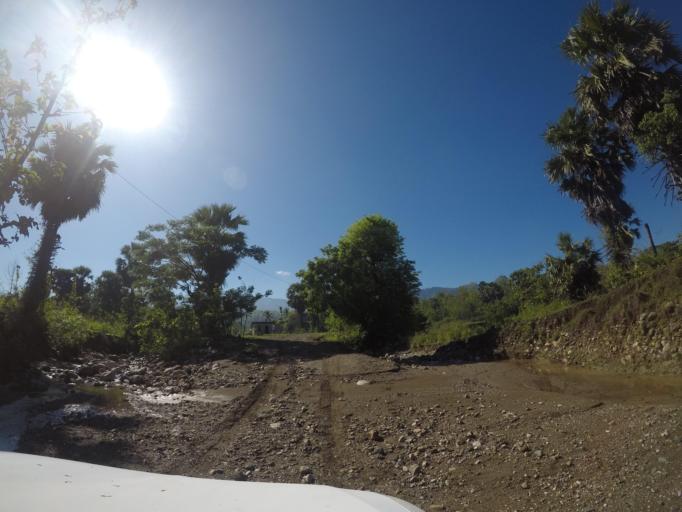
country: TL
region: Bobonaro
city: Maliana
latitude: -8.9949
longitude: 125.2038
